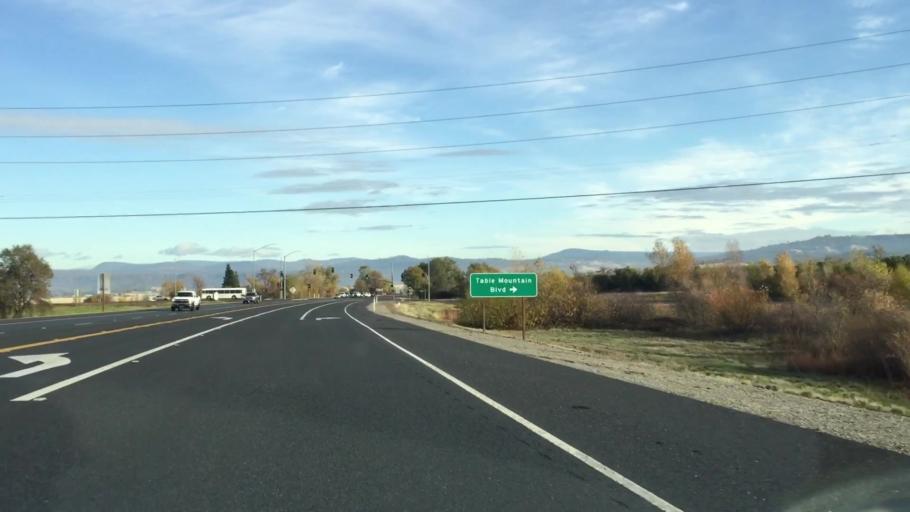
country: US
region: California
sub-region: Butte County
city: Thermalito
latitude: 39.6006
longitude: -121.6195
